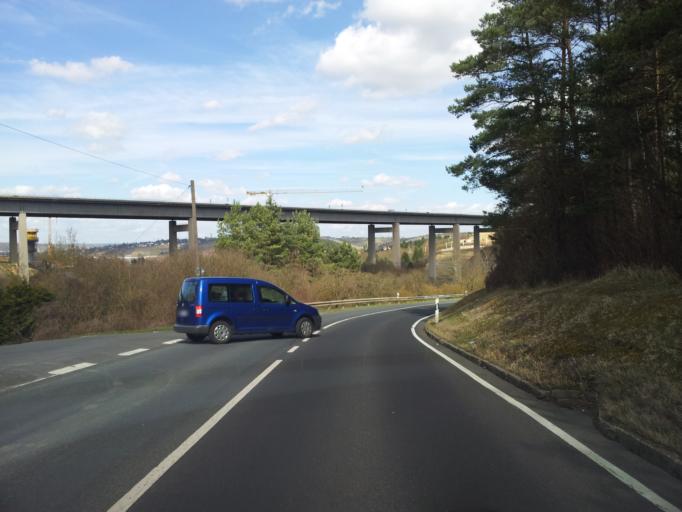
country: DE
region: Bavaria
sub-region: Regierungsbezirk Unterfranken
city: Reichenberg
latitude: 49.7490
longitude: 9.9388
